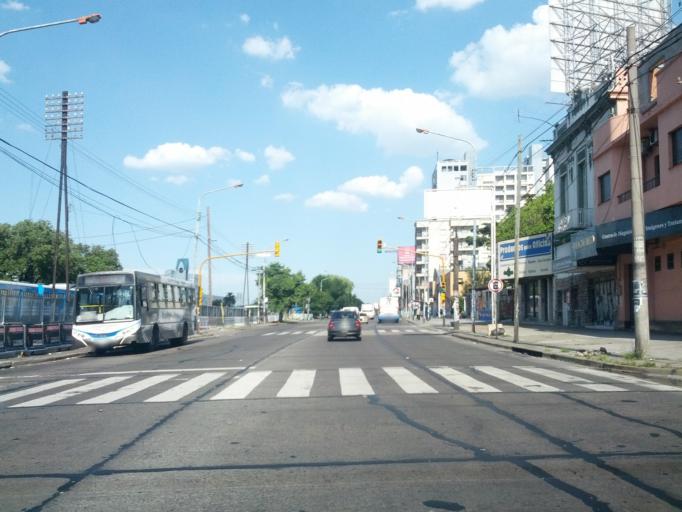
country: AR
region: Buenos Aires
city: San Justo
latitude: -34.6400
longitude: -58.5587
